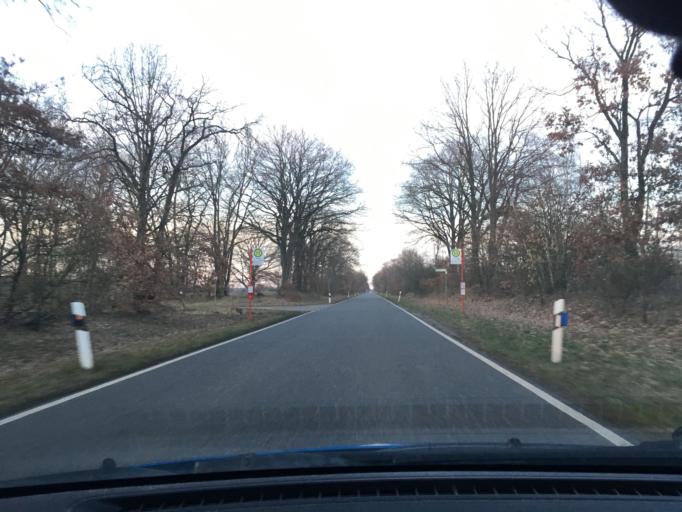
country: DE
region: Schleswig-Holstein
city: Langenlehsten
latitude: 53.5052
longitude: 10.7422
